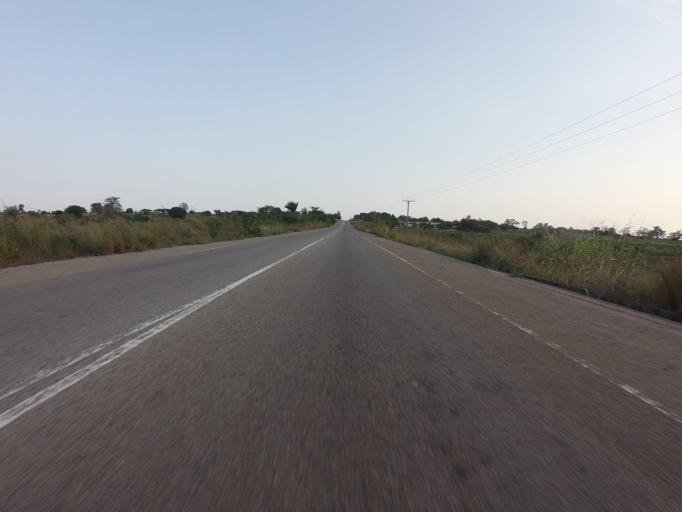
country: GH
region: Volta
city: Anloga
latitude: 6.0563
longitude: 0.6045
